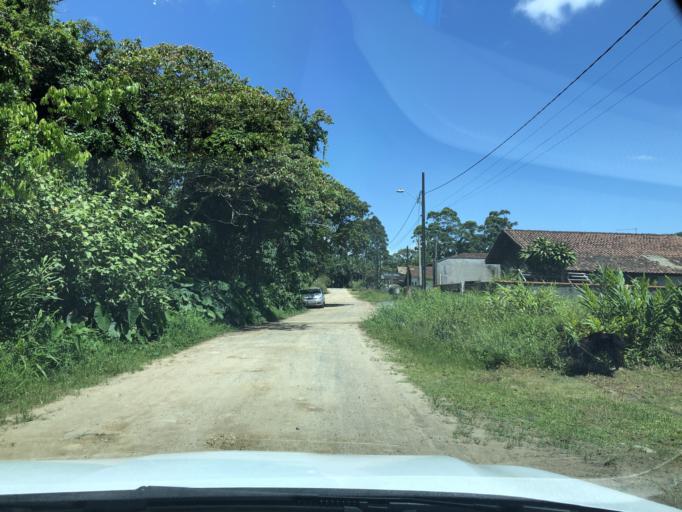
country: BR
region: Santa Catarina
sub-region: Sao Francisco Do Sul
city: Sao Francisco do Sul
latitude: -26.2091
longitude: -48.5367
